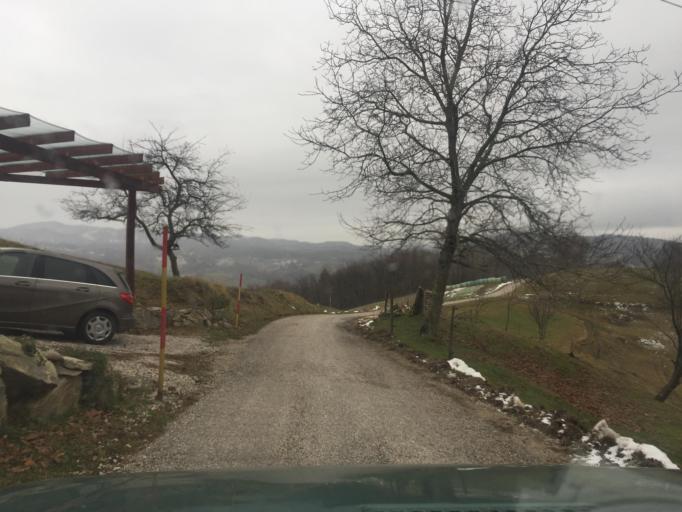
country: SI
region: Kanal
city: Kanal
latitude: 46.0710
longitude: 13.6929
